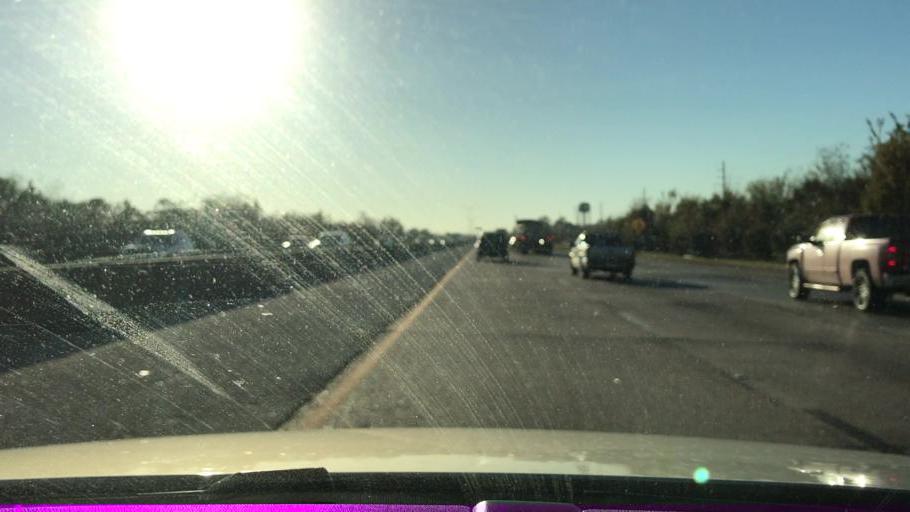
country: US
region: Texas
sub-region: Harris County
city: Channelview
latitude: 29.7885
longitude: -95.0967
